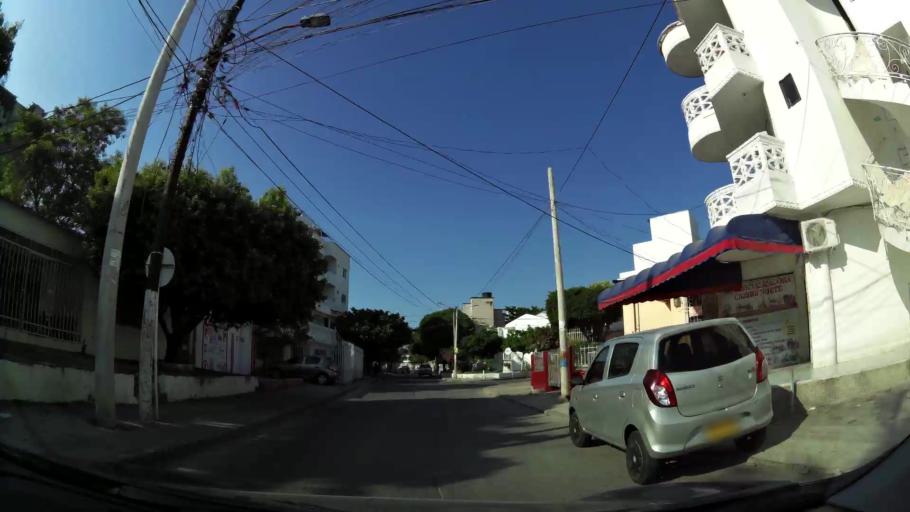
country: CO
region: Bolivar
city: Cartagena
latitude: 10.3964
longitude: -75.4840
